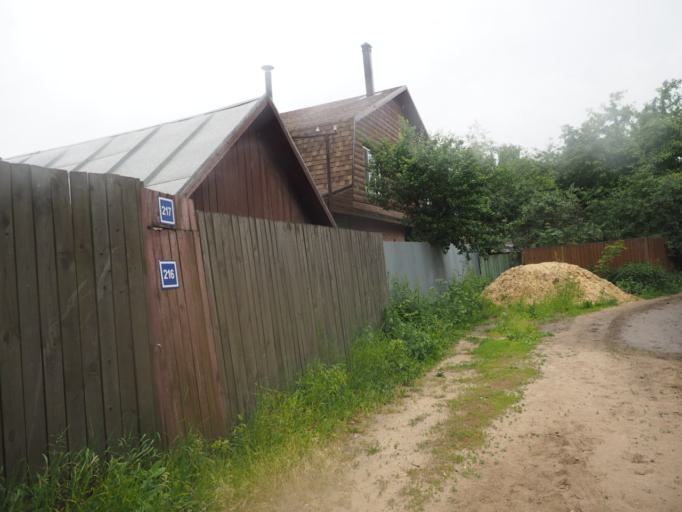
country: RU
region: Moskovskaya
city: Lyubertsy
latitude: 55.6450
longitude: 37.8871
